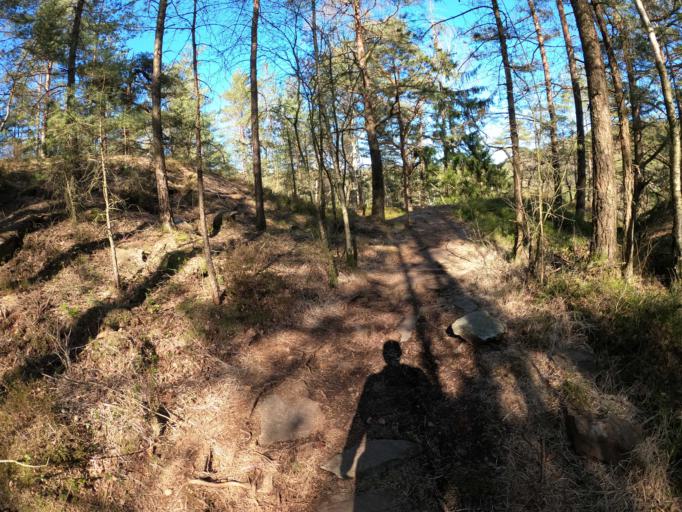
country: SE
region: Vaestra Goetaland
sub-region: Harryda Kommun
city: Molnlycke
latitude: 57.6396
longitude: 12.1143
